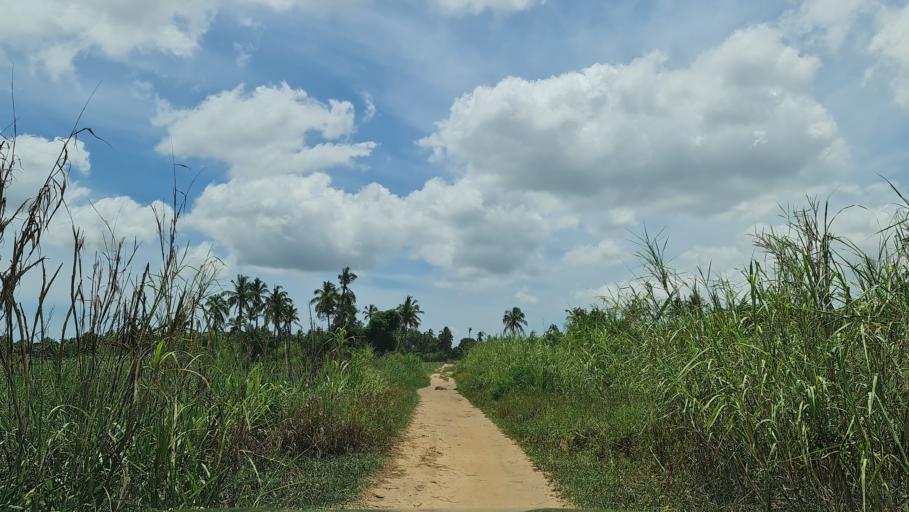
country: MZ
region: Zambezia
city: Quelimane
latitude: -17.5734
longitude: 37.3738
